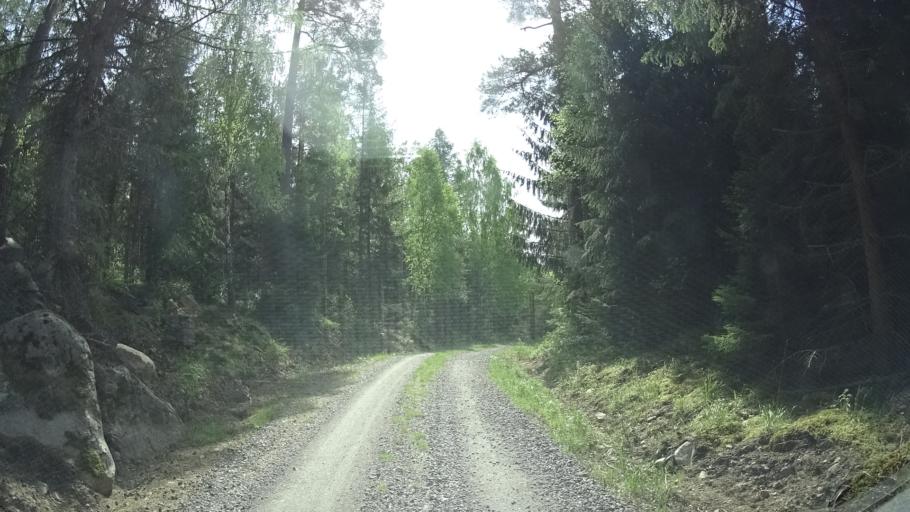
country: SE
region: OEstergoetland
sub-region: Finspangs Kommun
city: Finspang
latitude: 58.8058
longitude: 15.8400
